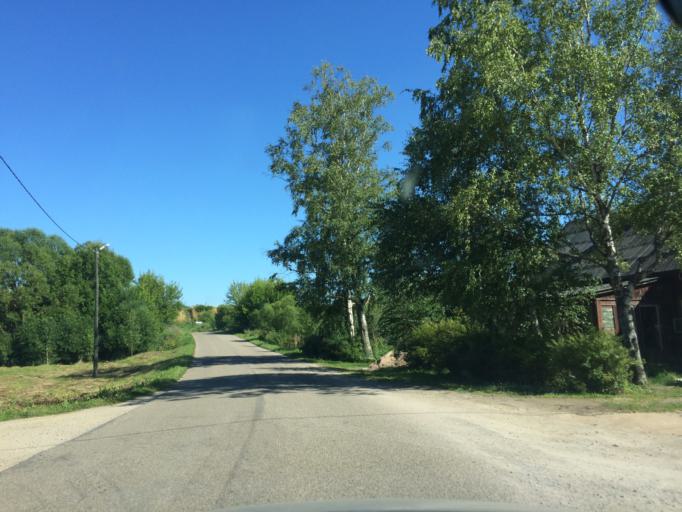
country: LV
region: Rezekne
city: Rezekne
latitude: 56.5081
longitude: 27.3144
